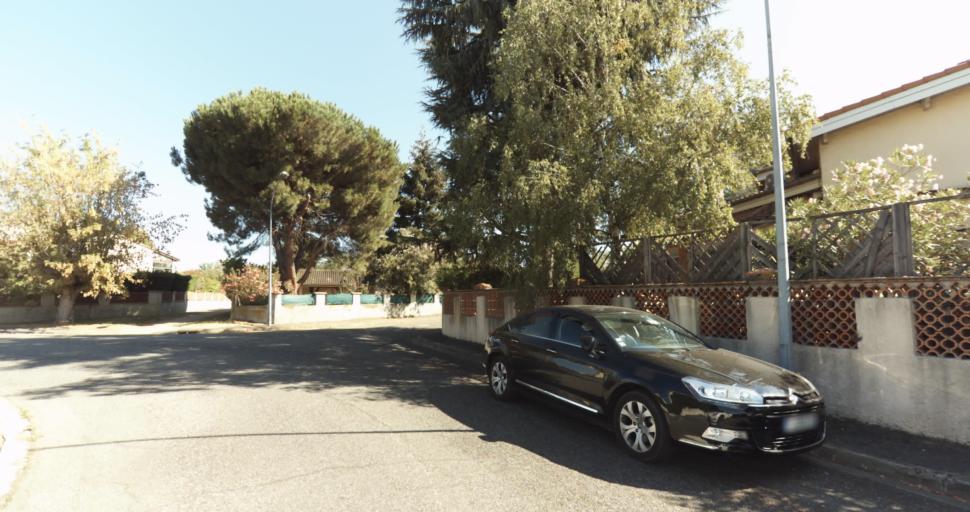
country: FR
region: Midi-Pyrenees
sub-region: Departement de la Haute-Garonne
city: L'Union
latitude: 43.6446
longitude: 1.4782
